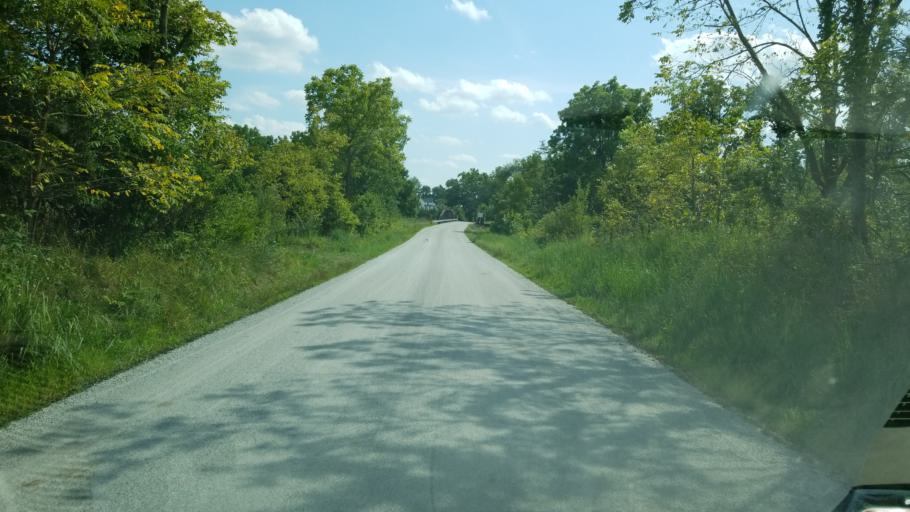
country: US
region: Ohio
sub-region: Hardin County
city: Kenton
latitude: 40.6233
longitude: -83.5302
